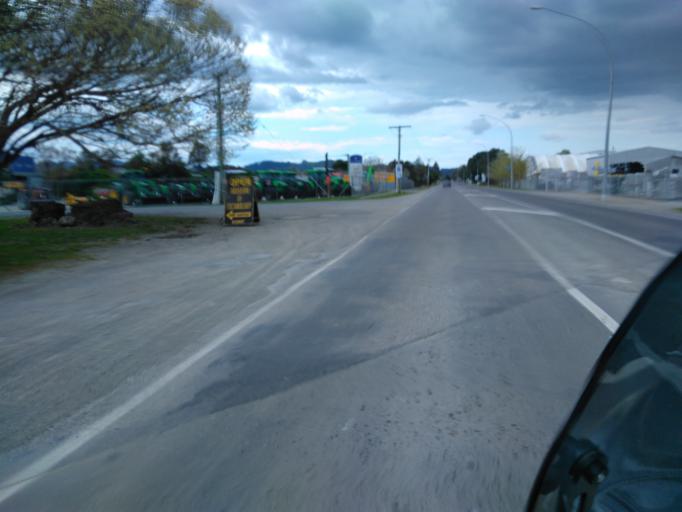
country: NZ
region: Gisborne
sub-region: Gisborne District
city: Gisborne
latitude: -38.6489
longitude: 177.9716
